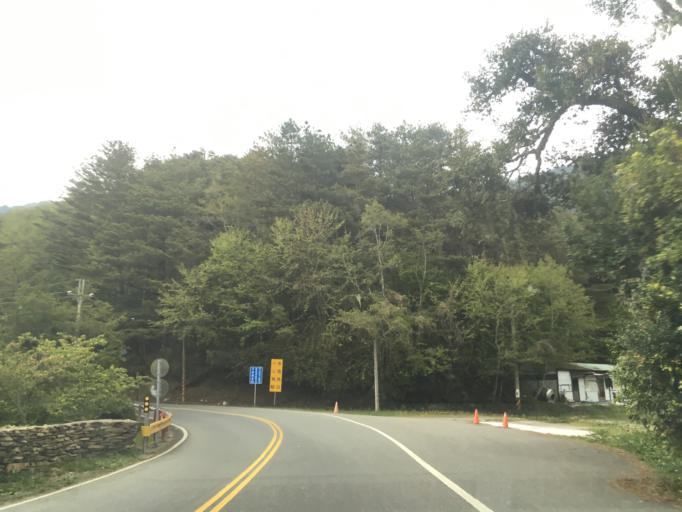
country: TW
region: Taiwan
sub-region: Hualien
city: Hualian
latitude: 24.1854
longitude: 121.3418
